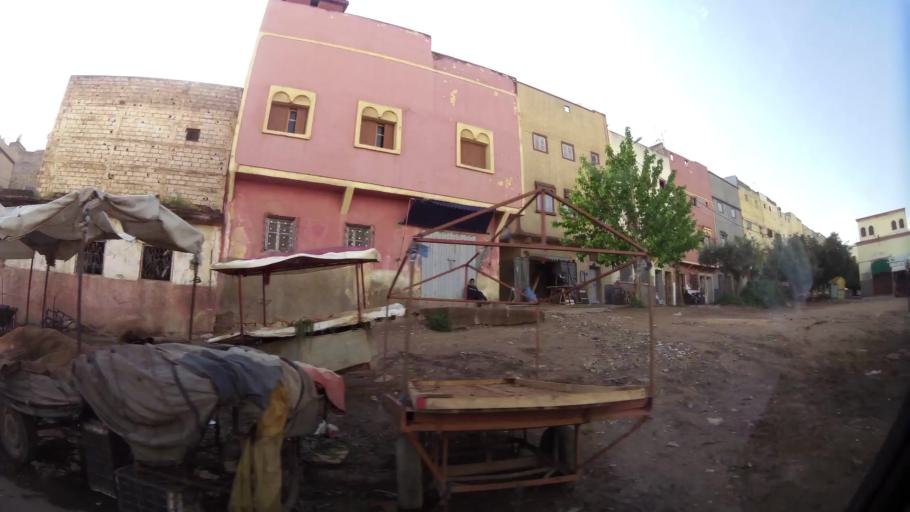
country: MA
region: Chaouia-Ouardigha
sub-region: Settat Province
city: Settat
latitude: 33.0049
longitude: -7.6281
